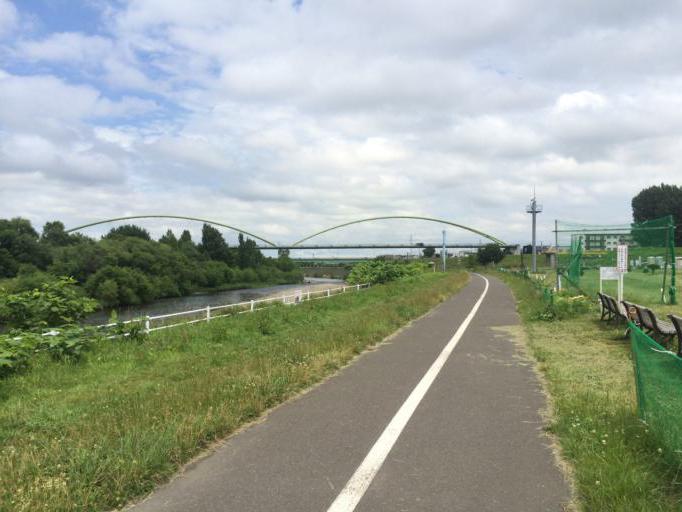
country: JP
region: Hokkaido
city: Sapporo
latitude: 43.0702
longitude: 141.4004
